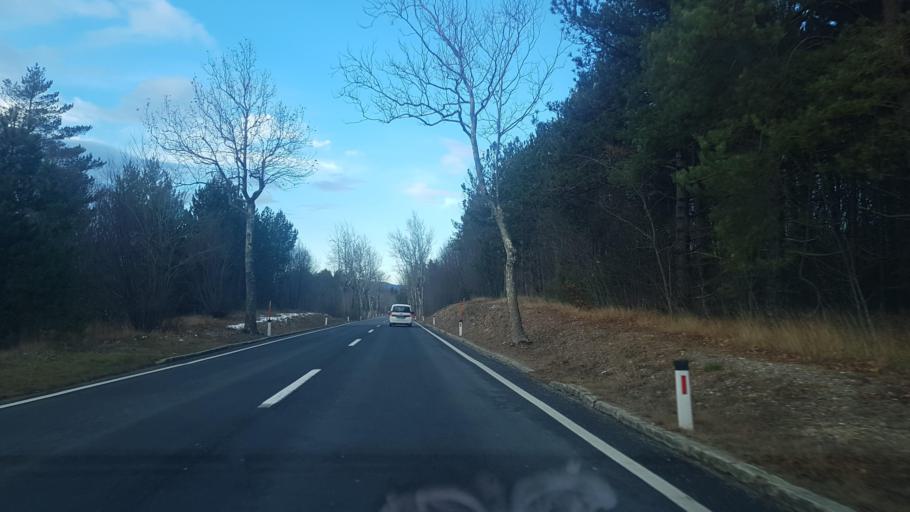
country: SI
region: Hrpelje-Kozina
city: Kozina
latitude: 45.5887
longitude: 13.9814
